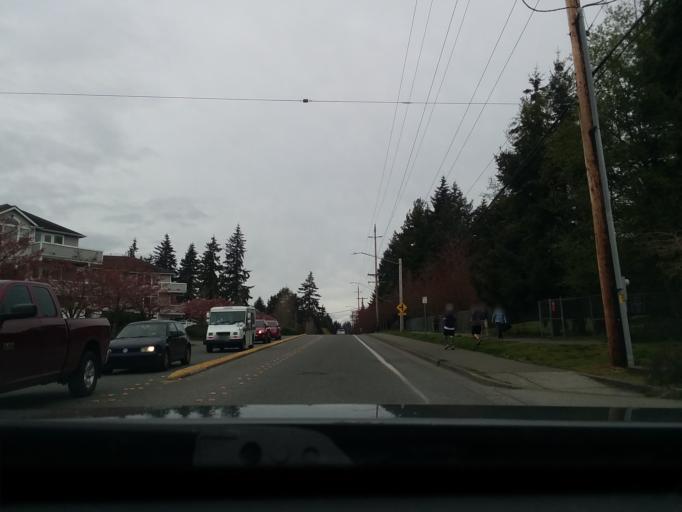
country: US
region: Washington
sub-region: Snohomish County
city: Lynnwood
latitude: 47.8105
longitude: -122.3258
